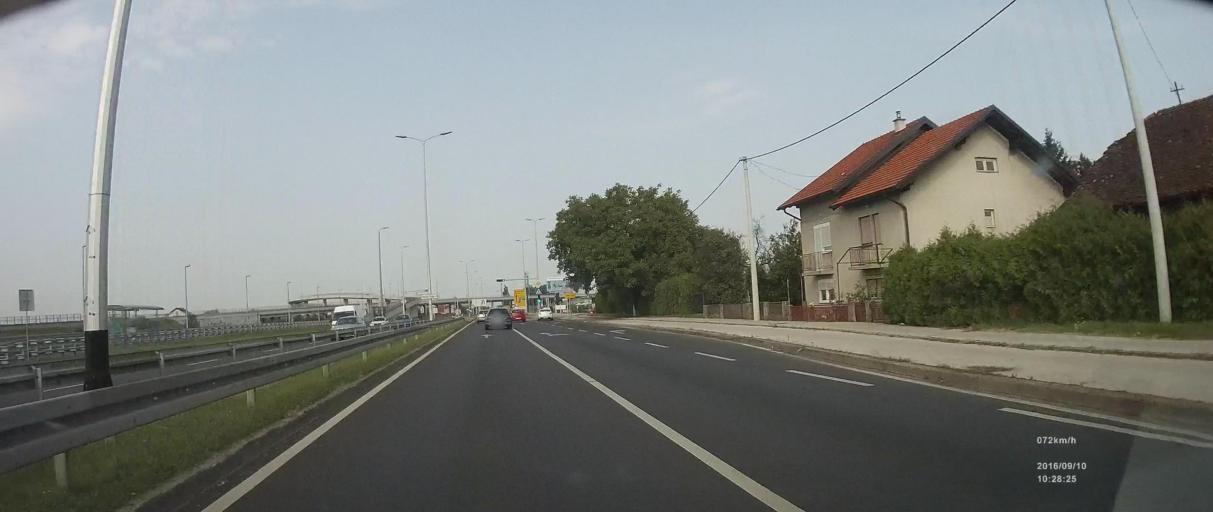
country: HR
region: Grad Zagreb
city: Odra
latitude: 45.7326
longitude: 16.0175
